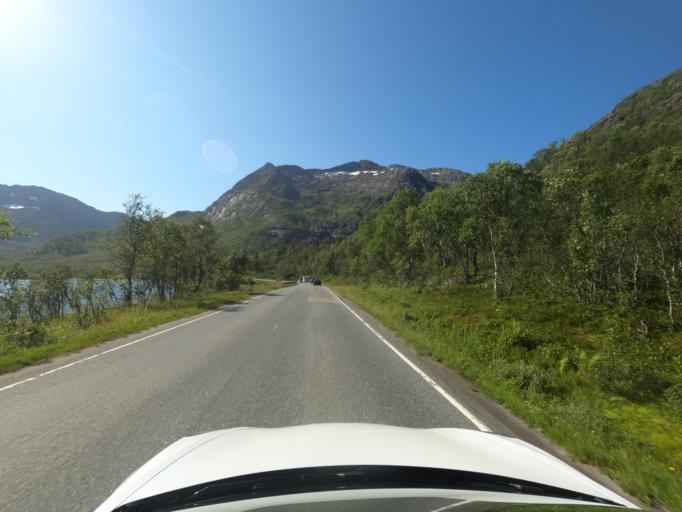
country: NO
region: Nordland
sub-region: Lodingen
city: Lodingen
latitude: 68.5382
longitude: 15.7231
